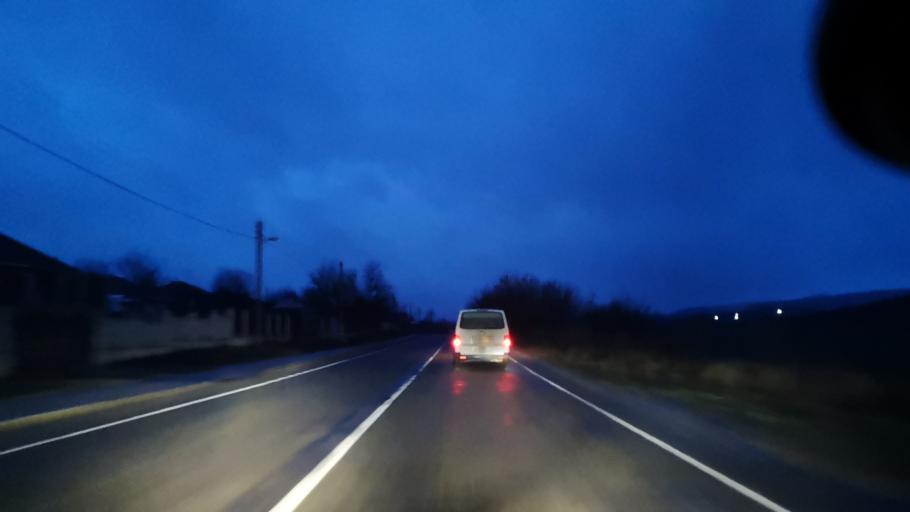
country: MD
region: Orhei
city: Orhei
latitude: 47.4488
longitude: 28.7928
